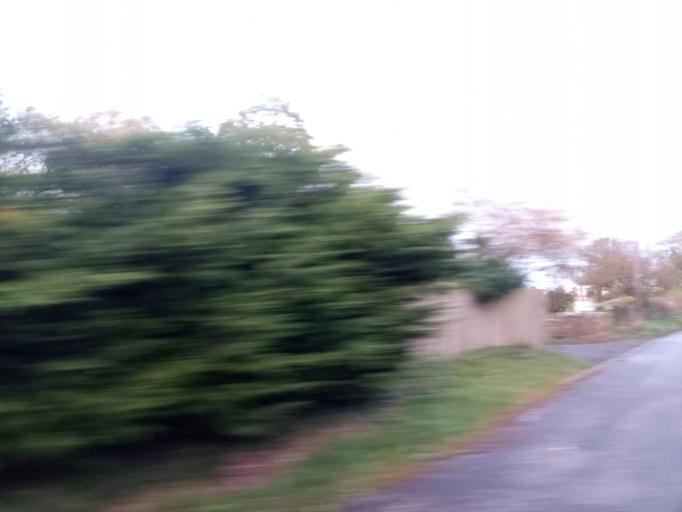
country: GB
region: Scotland
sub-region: Midlothian
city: Gorebridge
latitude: 55.8841
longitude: -3.0256
